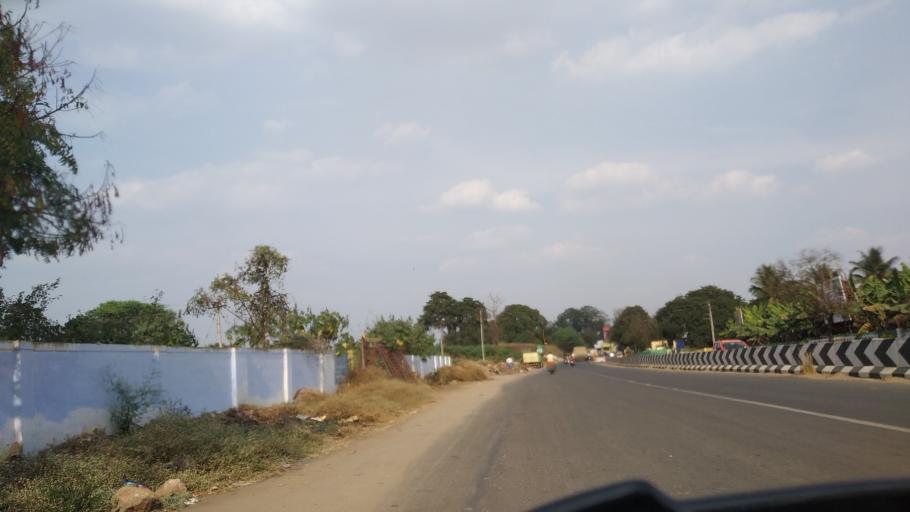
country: IN
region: Tamil Nadu
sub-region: Coimbatore
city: Perur
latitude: 10.9705
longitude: 76.9100
